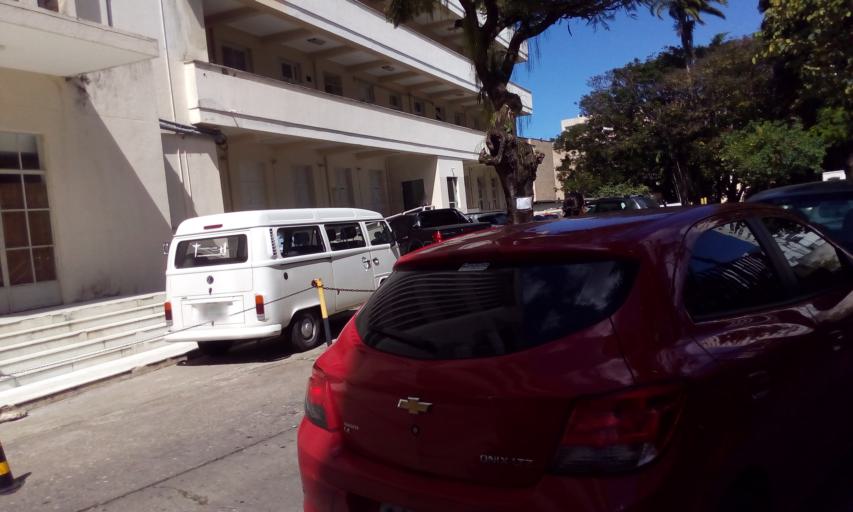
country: BR
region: Bahia
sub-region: Salvador
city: Salvador
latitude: -12.9931
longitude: -38.5205
